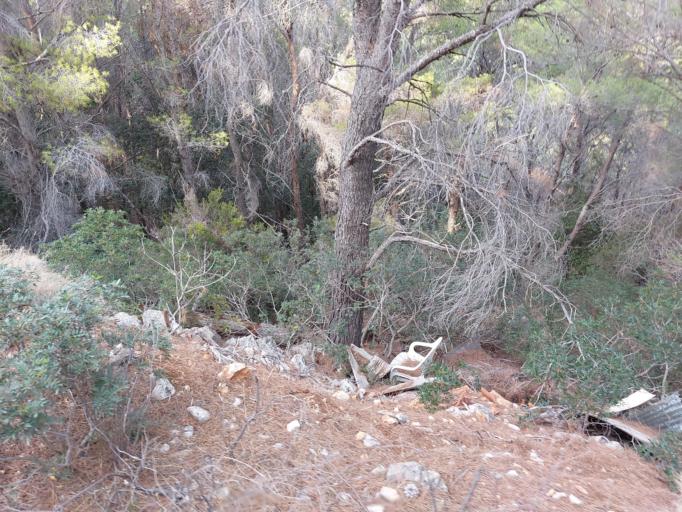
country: HR
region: Dubrovacko-Neretvanska
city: Smokvica
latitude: 42.7346
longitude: 16.8323
